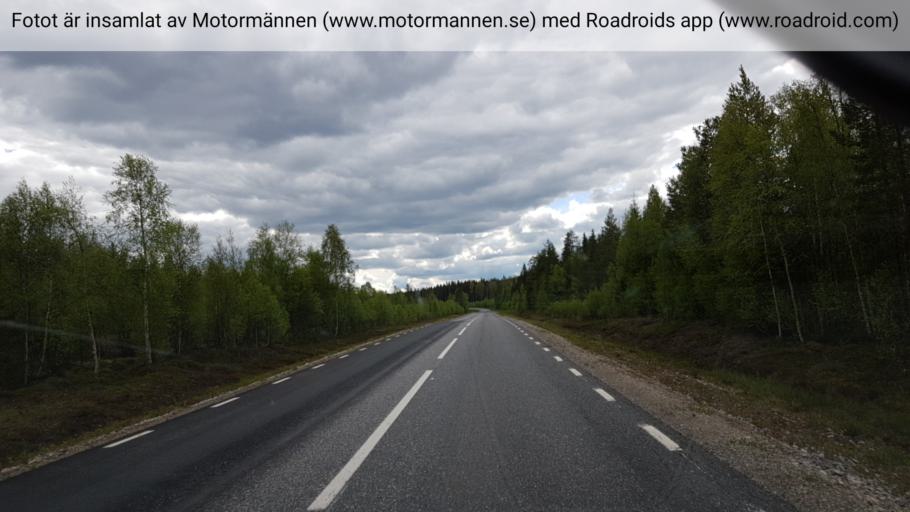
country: SE
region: Vaesterbotten
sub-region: Skelleftea Kommun
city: Langsele
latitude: 64.5807
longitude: 19.9276
